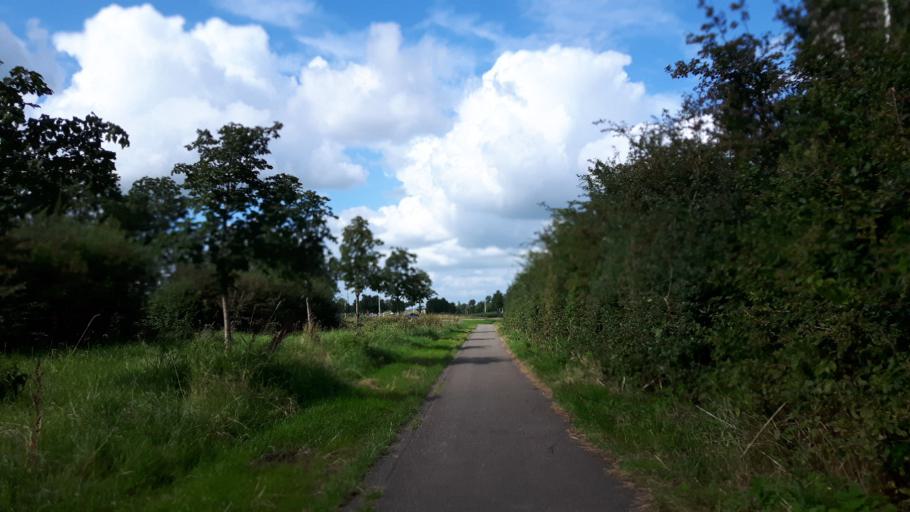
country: NL
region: Utrecht
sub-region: Stichtse Vecht
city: Spechtenkamp
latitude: 52.0832
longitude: 5.0040
